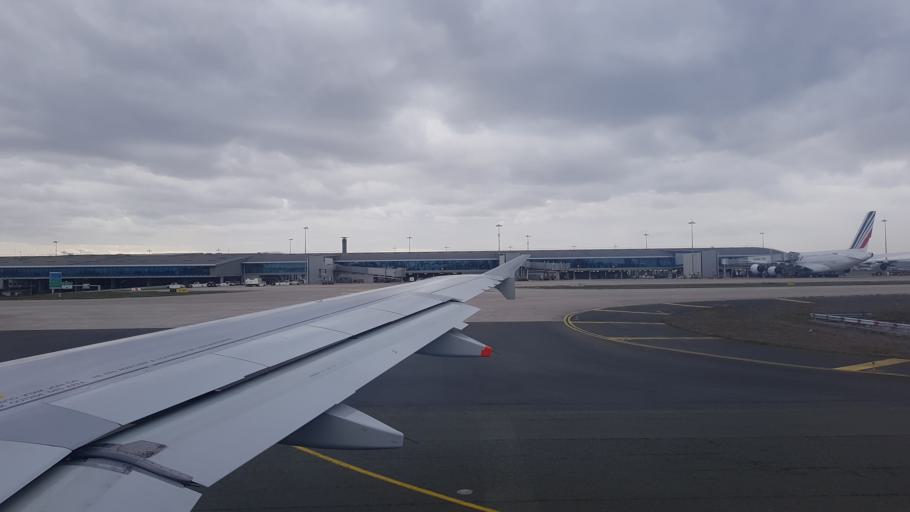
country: FR
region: Ile-de-France
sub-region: Departement de Seine-et-Marne
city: Mitry-Mory
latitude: 49.0067
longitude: 2.5956
